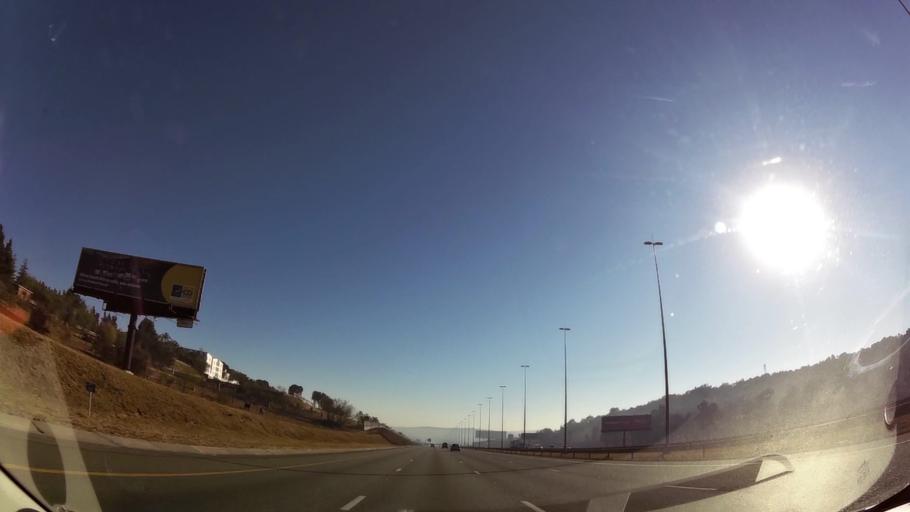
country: ZA
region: Gauteng
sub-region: City of Tshwane Metropolitan Municipality
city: Centurion
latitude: -25.8957
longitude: 28.2546
